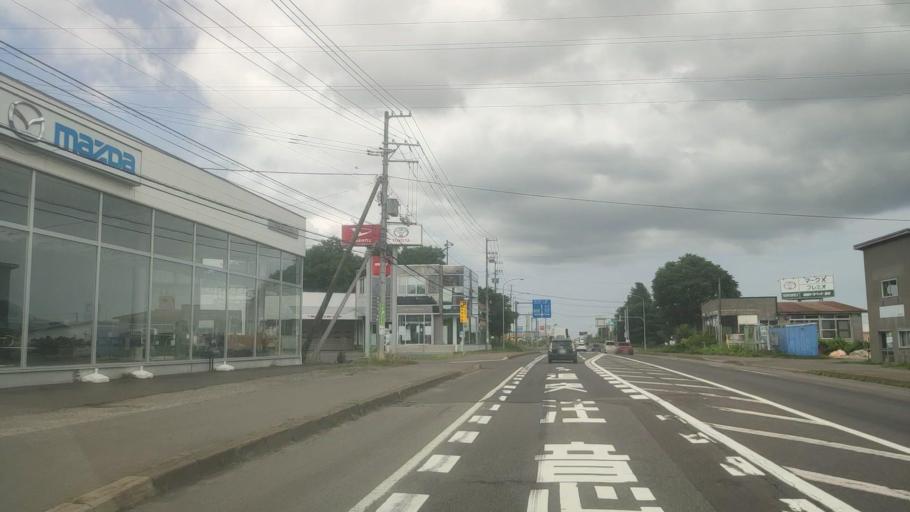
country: JP
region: Hokkaido
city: Nanae
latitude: 42.0917
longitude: 140.5783
